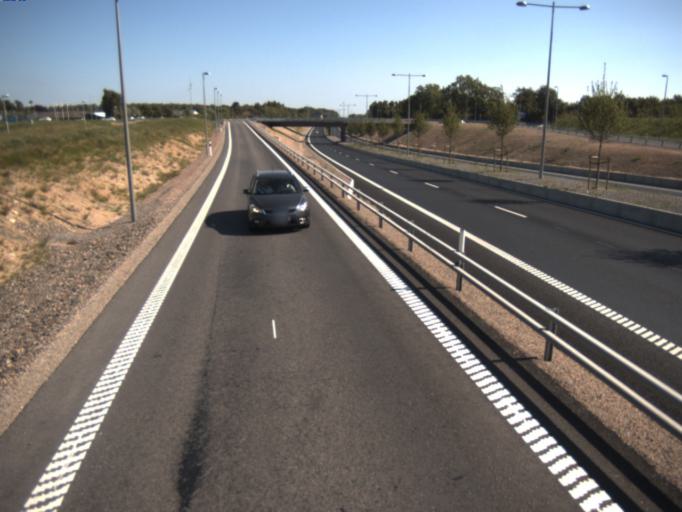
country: SE
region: Skane
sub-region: Helsingborg
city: Odakra
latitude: 56.0655
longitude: 12.7447
